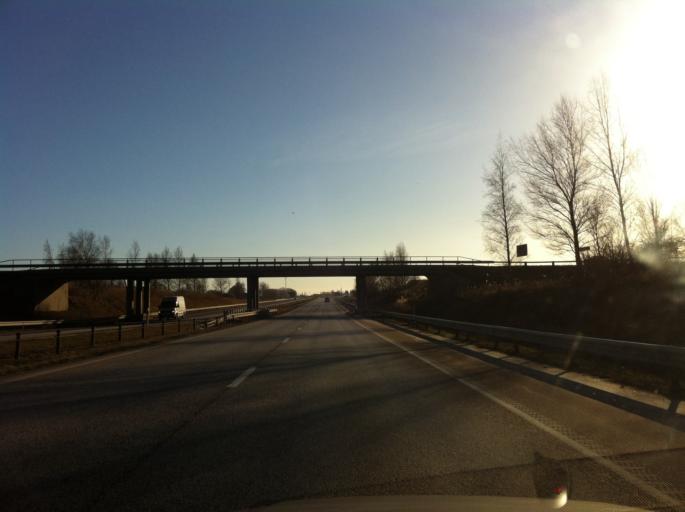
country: SE
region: Skane
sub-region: Angelholms Kommun
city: AEngelholm
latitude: 56.1965
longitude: 12.8601
